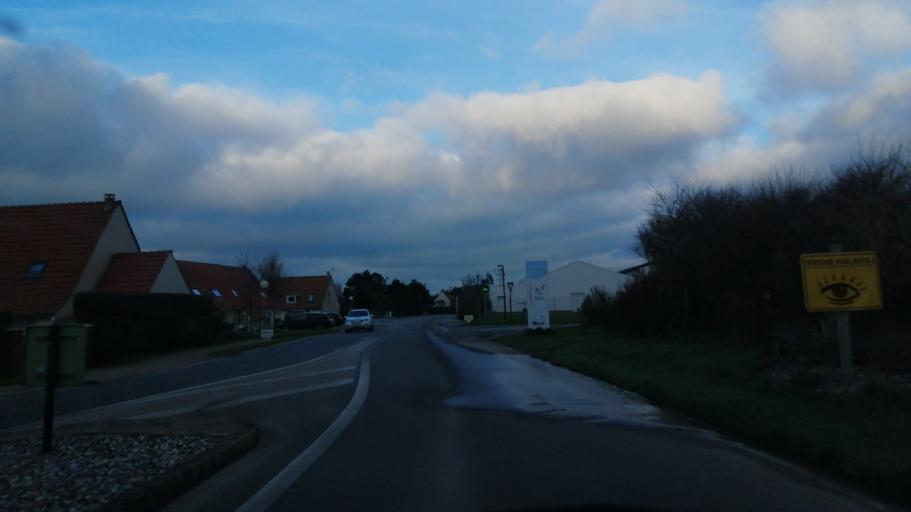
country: FR
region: Nord-Pas-de-Calais
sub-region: Departement du Pas-de-Calais
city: Ambleteuse
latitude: 50.8485
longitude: 1.6086
